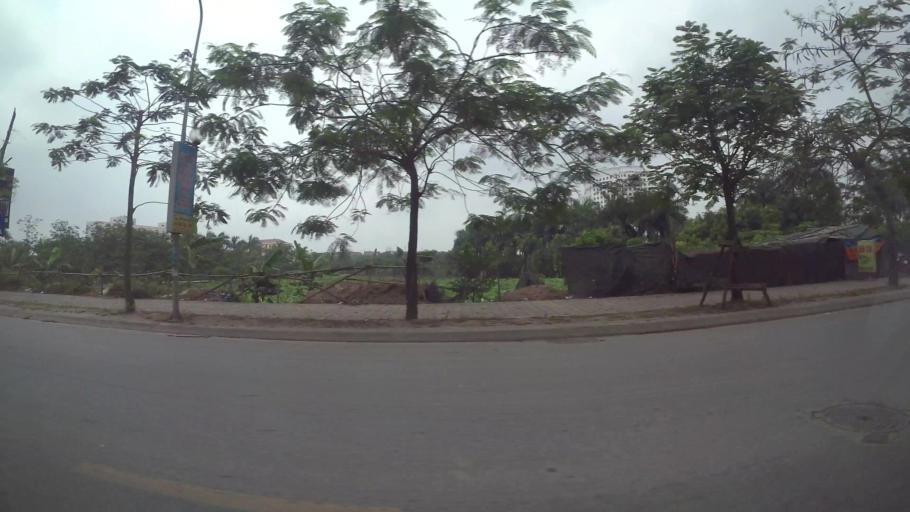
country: VN
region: Ha Noi
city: Trau Quy
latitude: 21.0578
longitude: 105.9164
